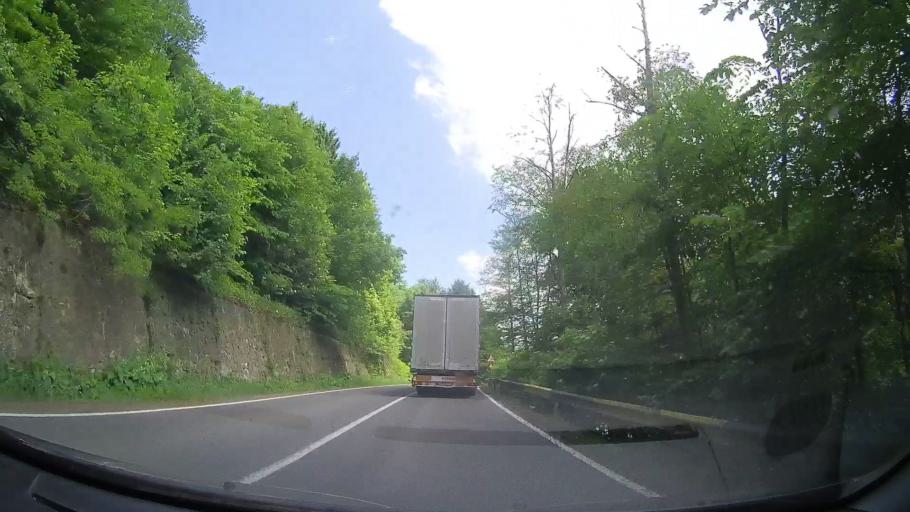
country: RO
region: Prahova
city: Maneciu
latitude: 45.3756
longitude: 25.9290
